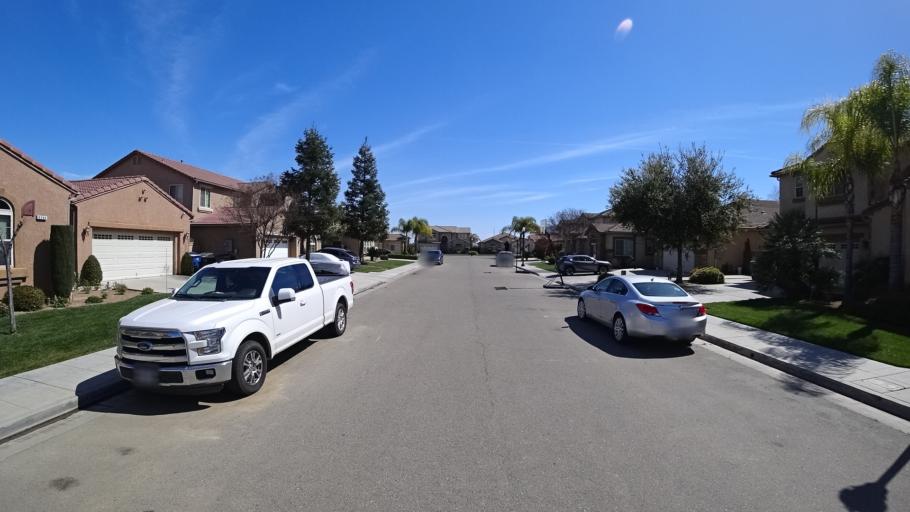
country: US
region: California
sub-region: Fresno County
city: Biola
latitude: 36.8204
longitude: -119.9092
